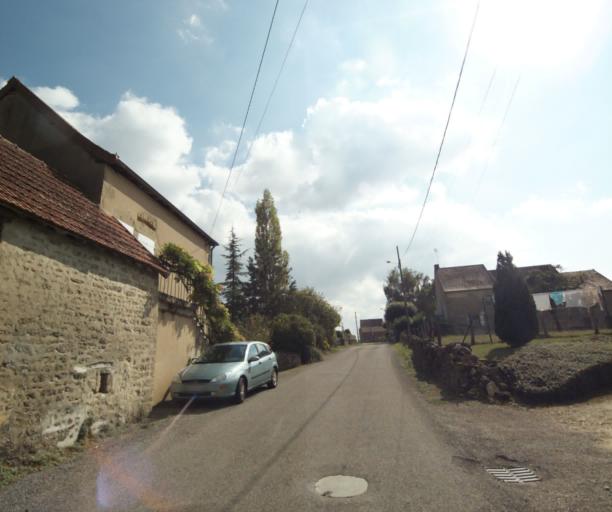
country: FR
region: Bourgogne
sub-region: Departement de Saone-et-Loire
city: Charolles
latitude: 46.3645
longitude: 4.2334
